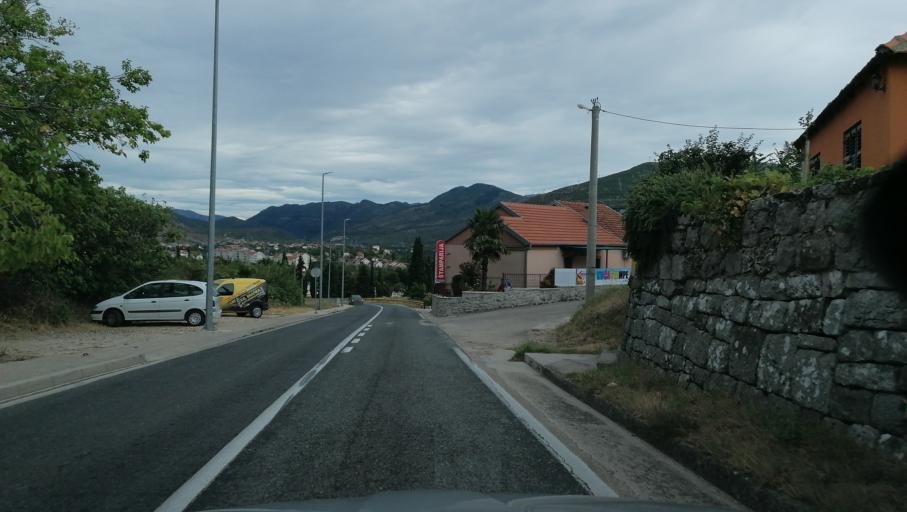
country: BA
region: Republika Srpska
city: Trebinje
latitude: 42.7208
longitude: 18.3474
